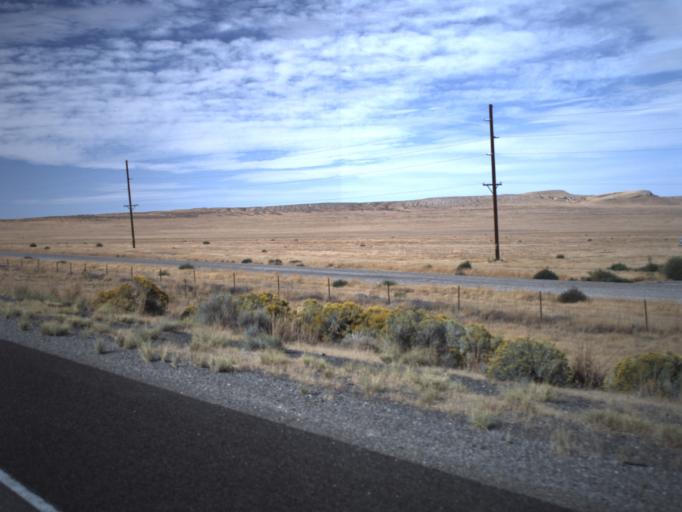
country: US
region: Utah
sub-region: Tooele County
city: Grantsville
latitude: 40.7839
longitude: -112.9642
